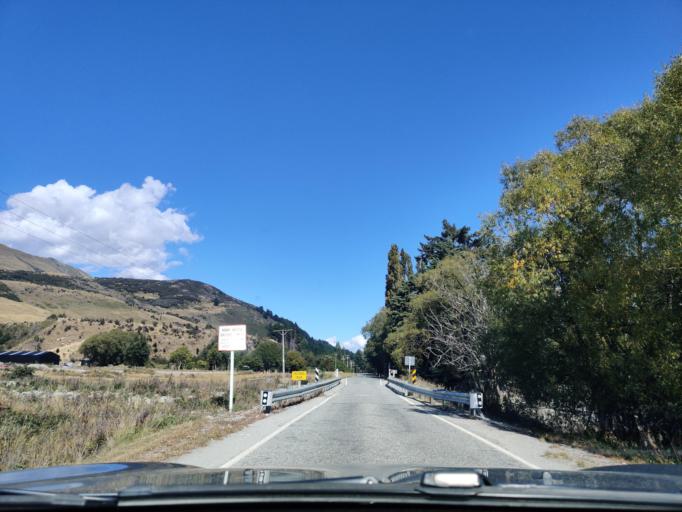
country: NZ
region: Otago
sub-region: Queenstown-Lakes District
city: Queenstown
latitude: -44.8001
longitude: 168.3985
